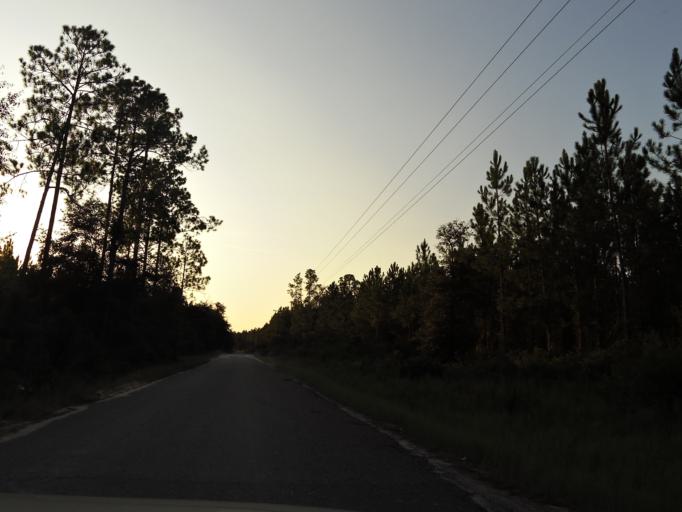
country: US
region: Florida
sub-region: Duval County
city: Baldwin
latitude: 30.3858
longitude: -82.0453
